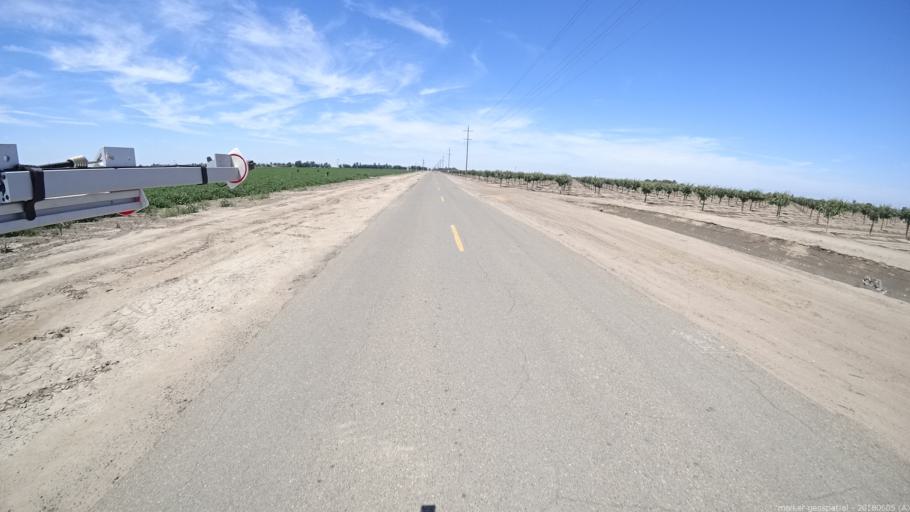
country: US
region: California
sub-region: Merced County
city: Dos Palos
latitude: 37.0872
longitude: -120.4734
